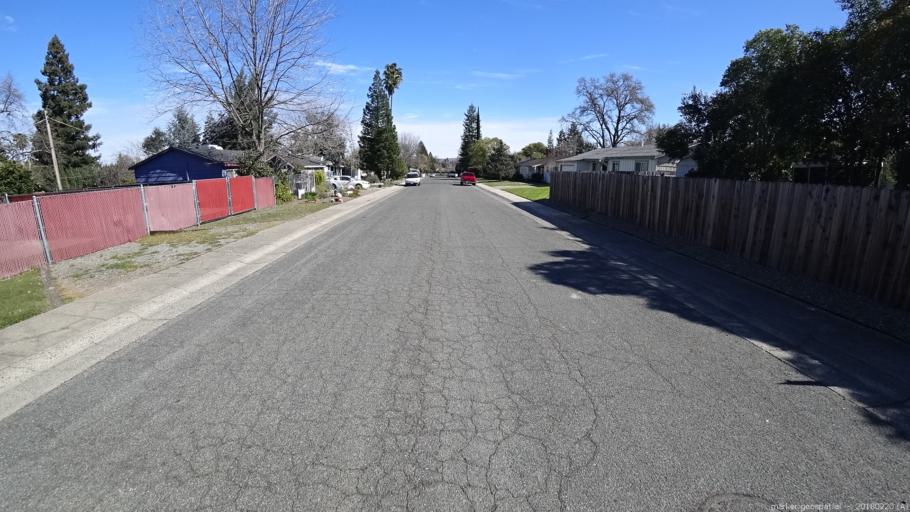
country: US
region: California
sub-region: Sacramento County
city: Orangevale
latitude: 38.6809
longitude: -121.2346
